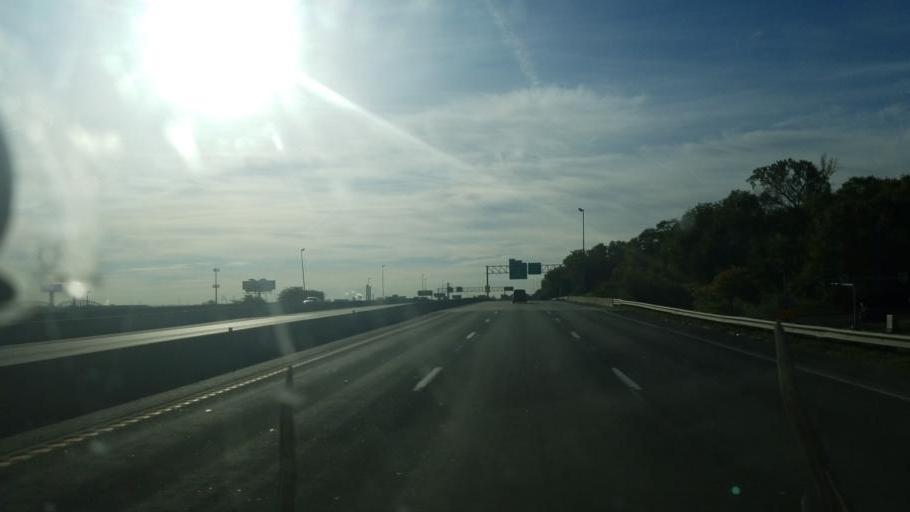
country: US
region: Illinois
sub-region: Madison County
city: Venice
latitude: 38.6737
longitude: -90.2050
